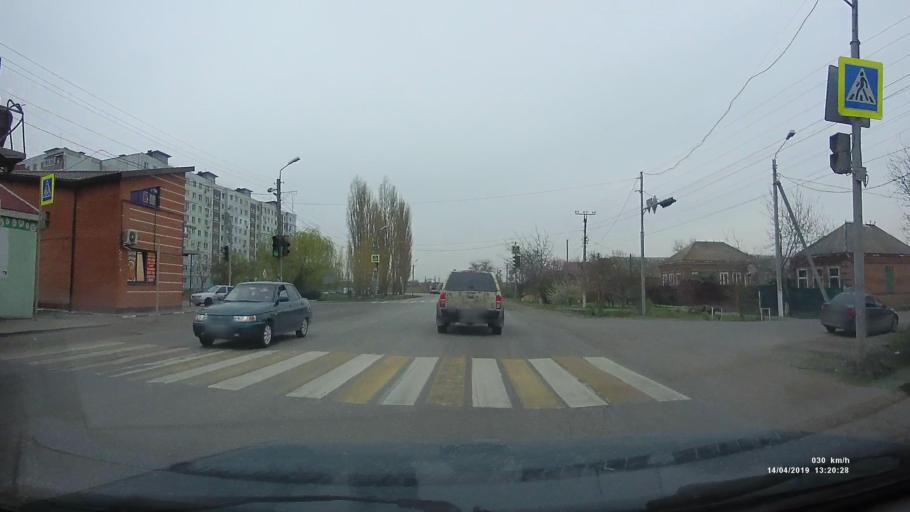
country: RU
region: Rostov
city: Kuleshovka
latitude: 47.0823
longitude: 39.5378
